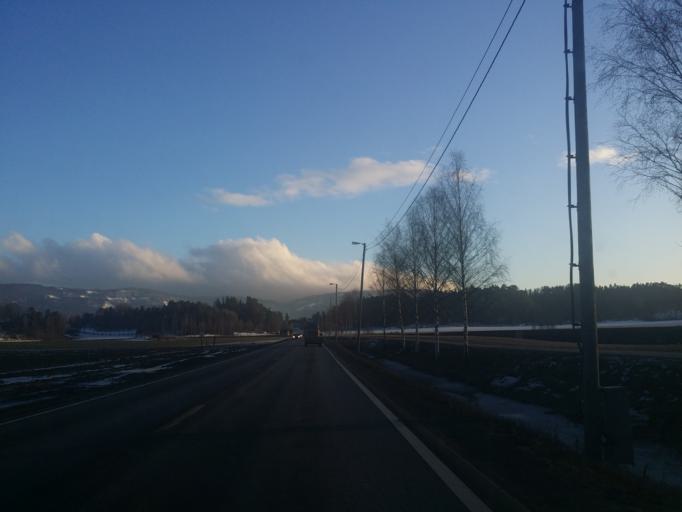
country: NO
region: Buskerud
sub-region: Hole
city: Vik
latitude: 60.1054
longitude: 10.2876
